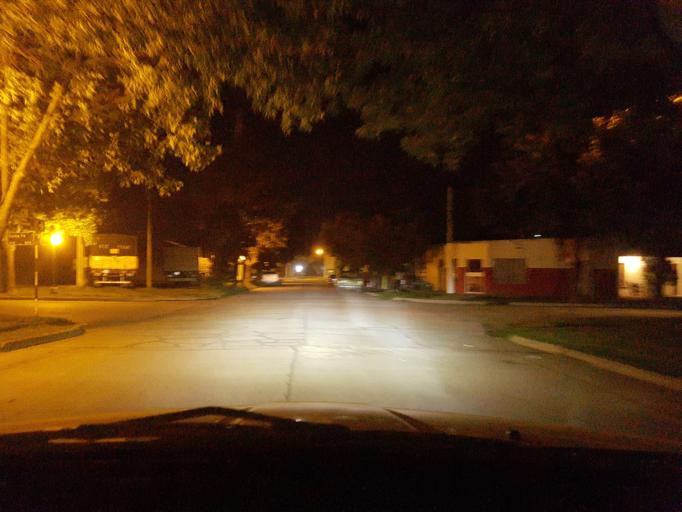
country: AR
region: Cordoba
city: General Cabrera
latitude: -32.7602
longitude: -63.7980
